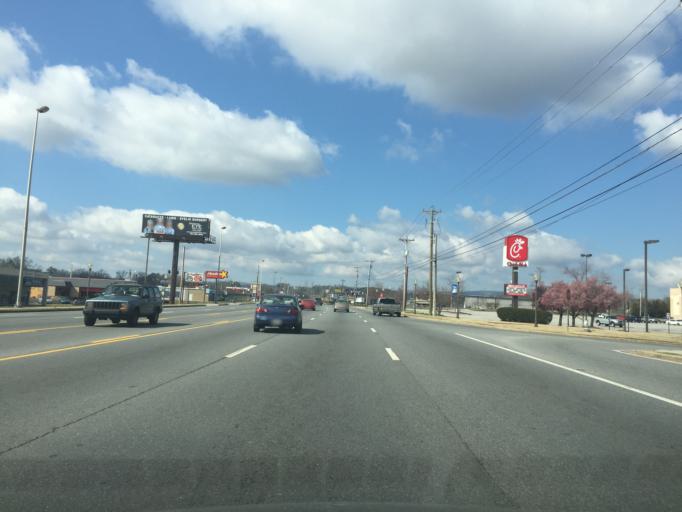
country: US
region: Georgia
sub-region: Catoosa County
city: Fort Oglethorpe
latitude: 34.9526
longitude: -85.2448
